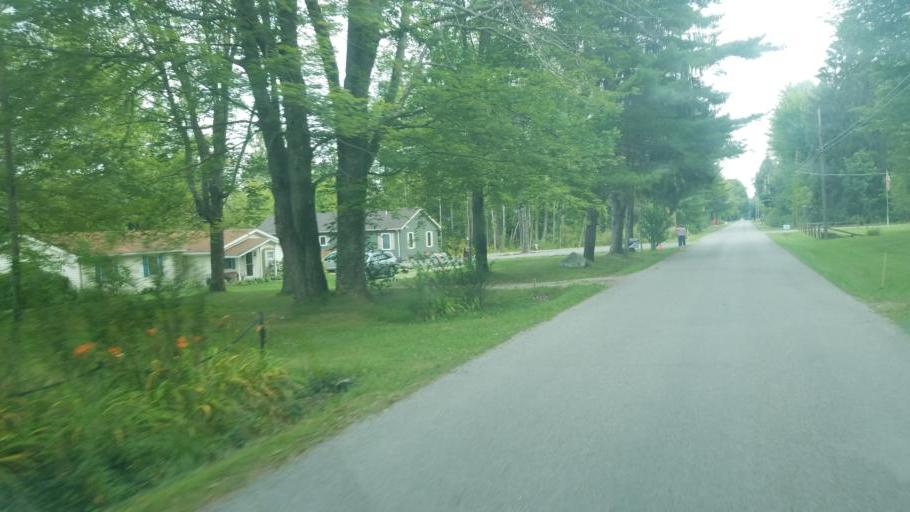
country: US
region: Pennsylvania
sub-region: Crawford County
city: Pymatuning Central
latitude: 41.6153
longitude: -80.5001
